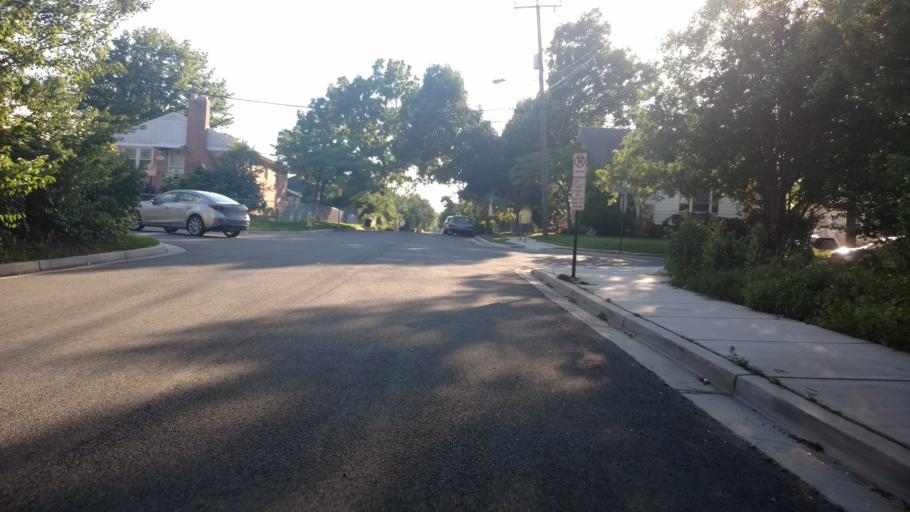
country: US
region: Virginia
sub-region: Arlington County
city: Arlington
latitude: 38.8666
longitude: -77.0814
